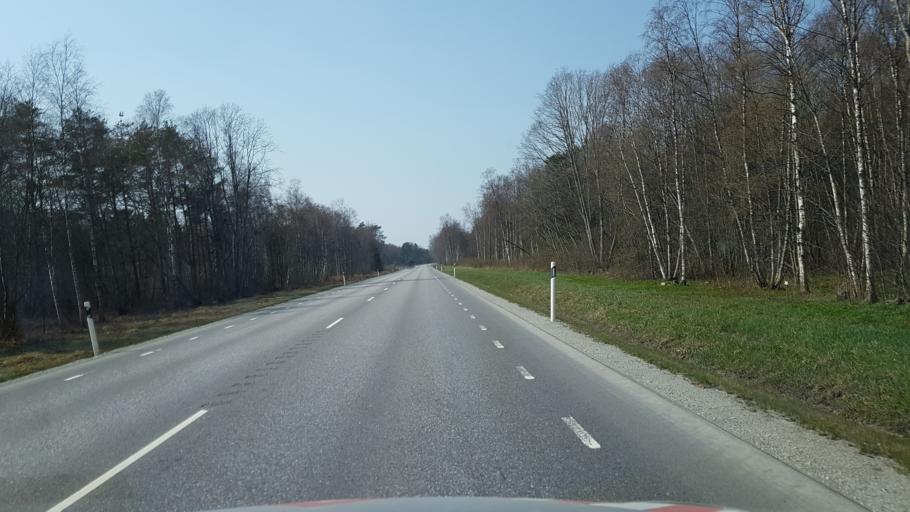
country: EE
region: Harju
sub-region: Paldiski linn
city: Paldiski
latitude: 59.3370
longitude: 24.2328
